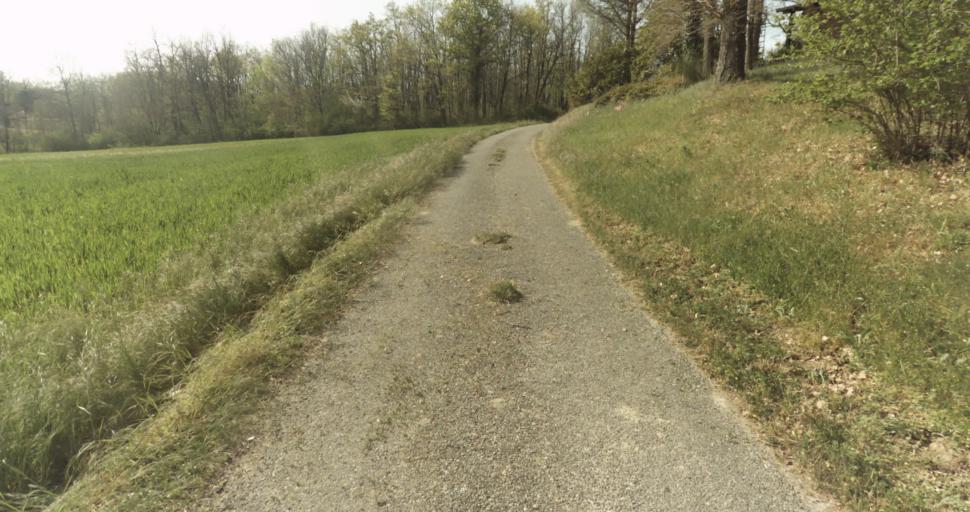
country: FR
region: Midi-Pyrenees
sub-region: Departement du Tarn-et-Garonne
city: Lafrancaise
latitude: 44.1496
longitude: 1.1795
